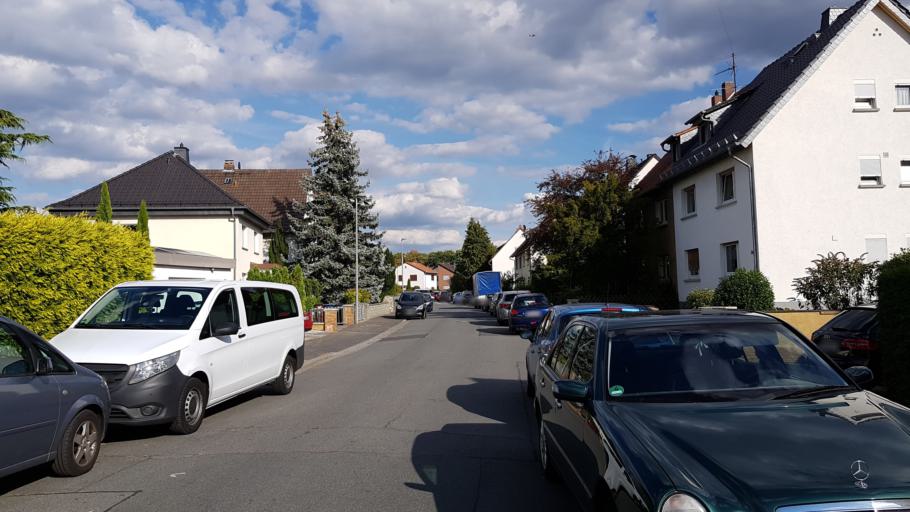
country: DE
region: Hesse
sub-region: Regierungsbezirk Darmstadt
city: Russelsheim
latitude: 49.9957
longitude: 8.4351
